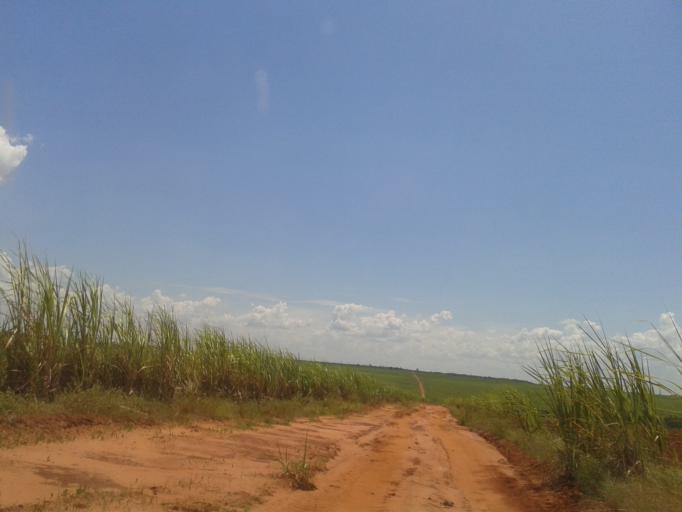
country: BR
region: Minas Gerais
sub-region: Santa Vitoria
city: Santa Vitoria
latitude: -19.1691
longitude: -50.4279
